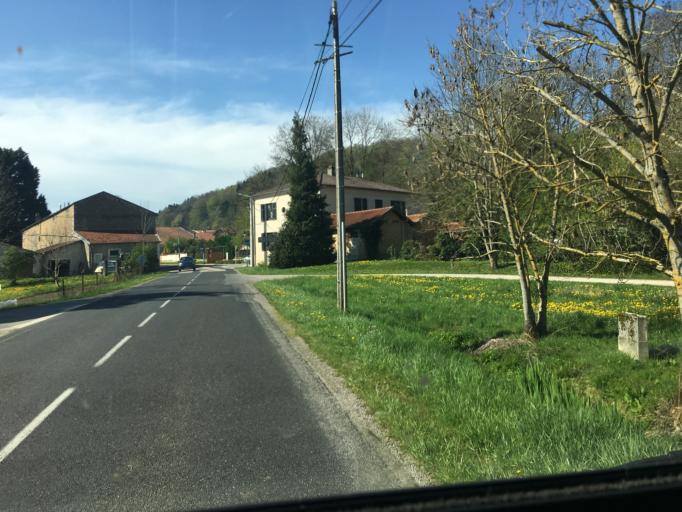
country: FR
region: Lorraine
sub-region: Departement de la Meuse
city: Vigneulles-les-Hattonchatel
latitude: 48.8979
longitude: 5.6600
